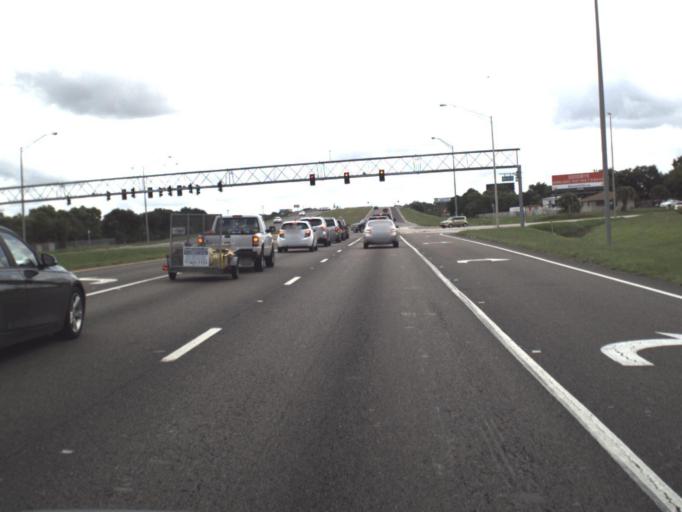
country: US
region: Florida
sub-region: Manatee County
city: West Samoset
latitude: 27.4802
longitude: -82.5559
